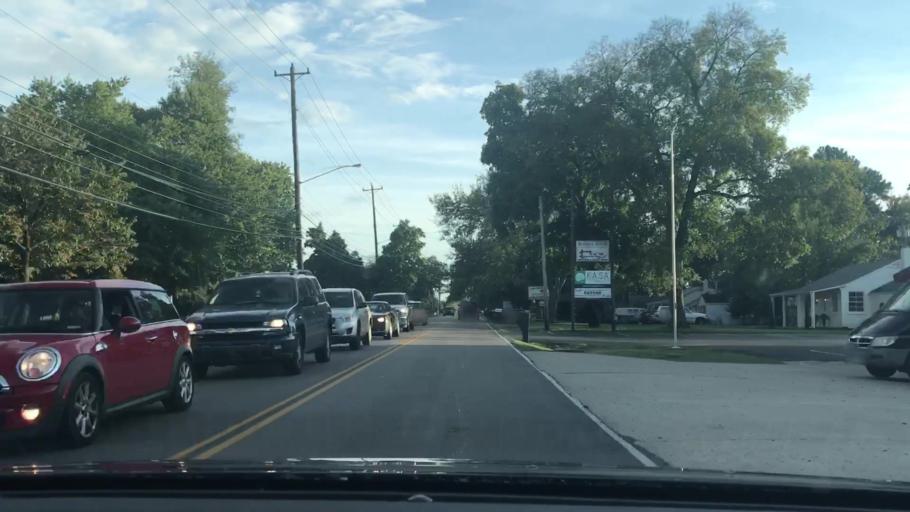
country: US
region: Tennessee
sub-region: Davidson County
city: Oak Hill
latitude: 36.1160
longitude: -86.7665
